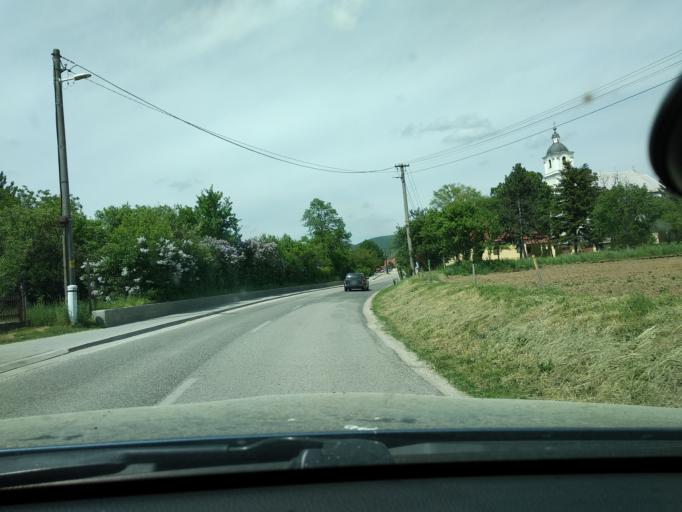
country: SK
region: Trenciansky
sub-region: Okres Nove Mesto nad Vahom
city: Nove Mesto nad Vahom
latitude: 48.8222
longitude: 17.8437
